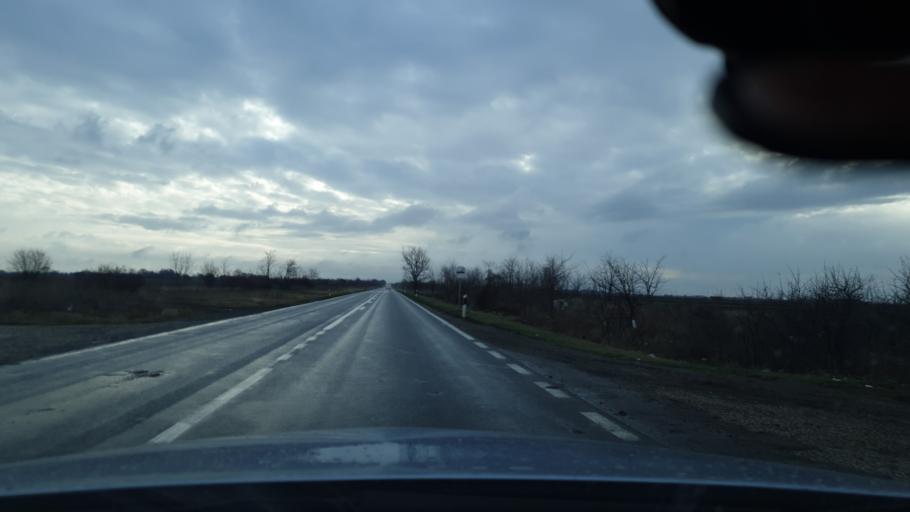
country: RS
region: Autonomna Pokrajina Vojvodina
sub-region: Juznobanatski Okrug
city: Kovin
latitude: 44.7735
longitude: 20.9406
